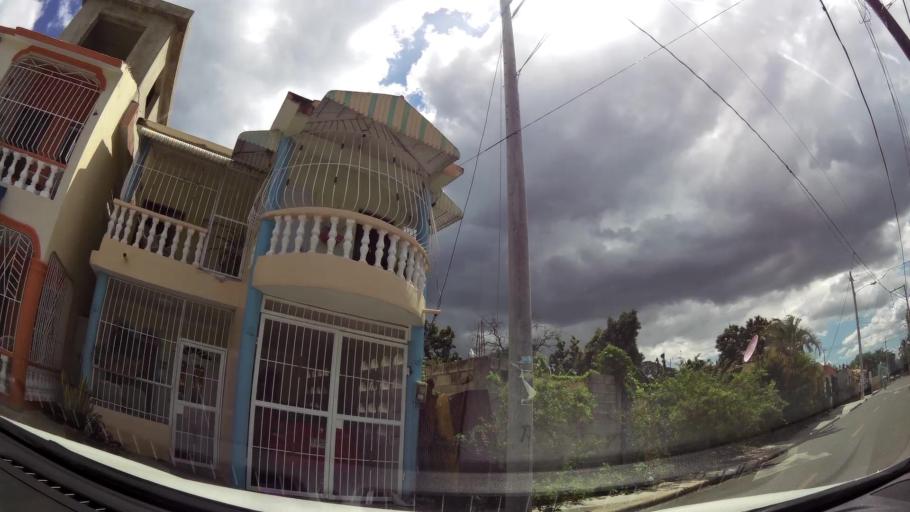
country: DO
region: San Cristobal
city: San Cristobal
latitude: 18.4204
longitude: -70.0909
